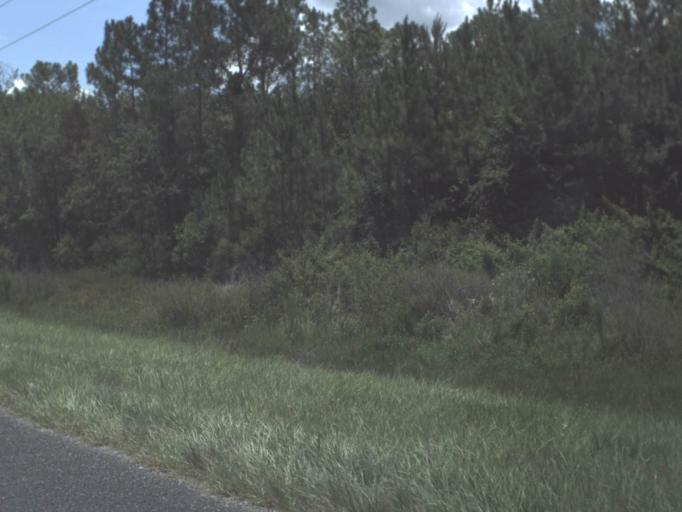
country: US
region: Florida
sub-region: Levy County
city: Bronson
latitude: 29.4741
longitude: -82.6797
